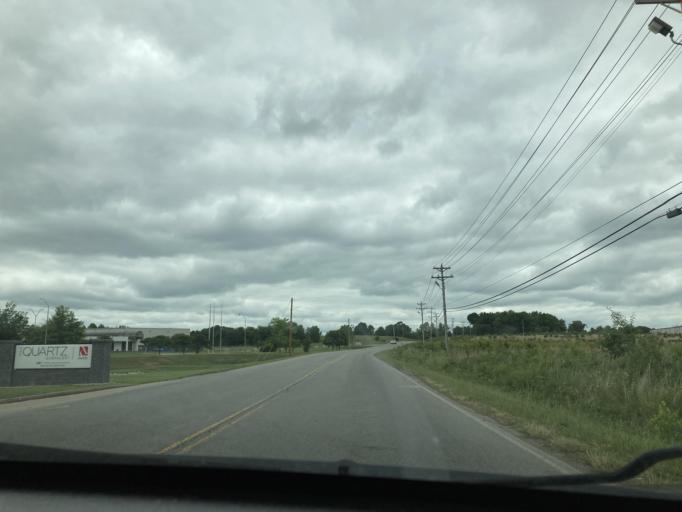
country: US
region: Tennessee
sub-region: Dickson County
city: Burns
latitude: 36.0480
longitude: -87.3437
